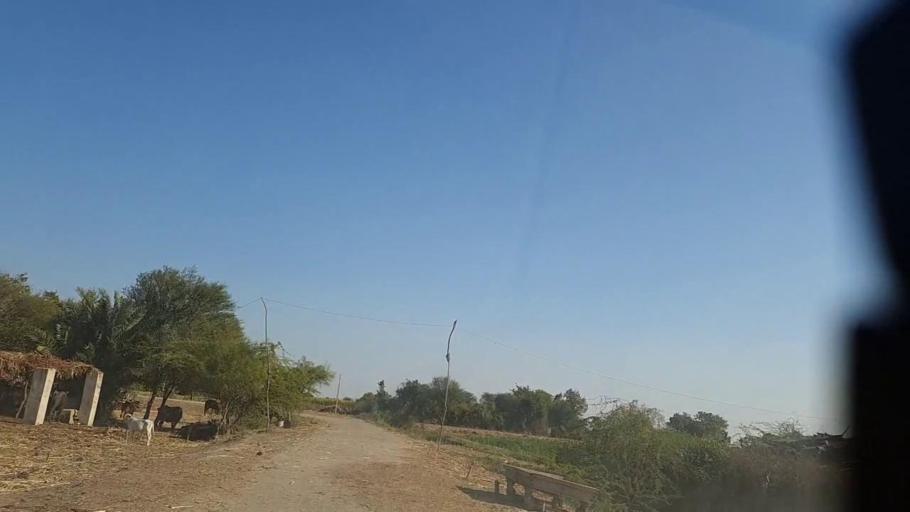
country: PK
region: Sindh
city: Digri
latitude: 25.1475
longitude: 69.0441
